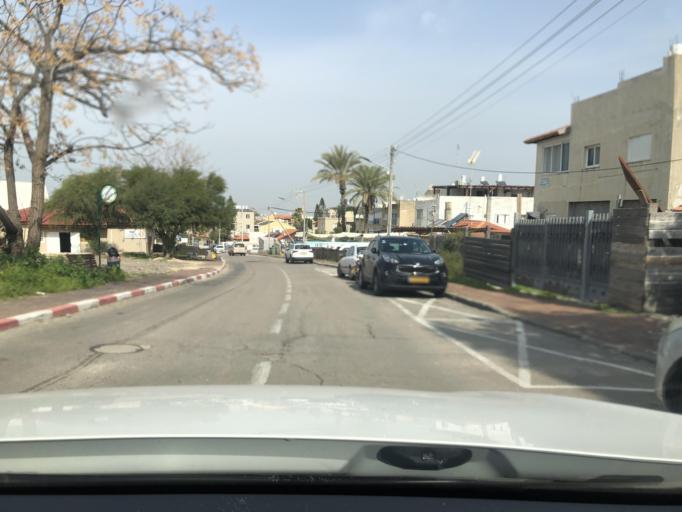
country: IL
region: Central District
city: Rosh Ha'Ayin
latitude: 32.0904
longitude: 34.9601
